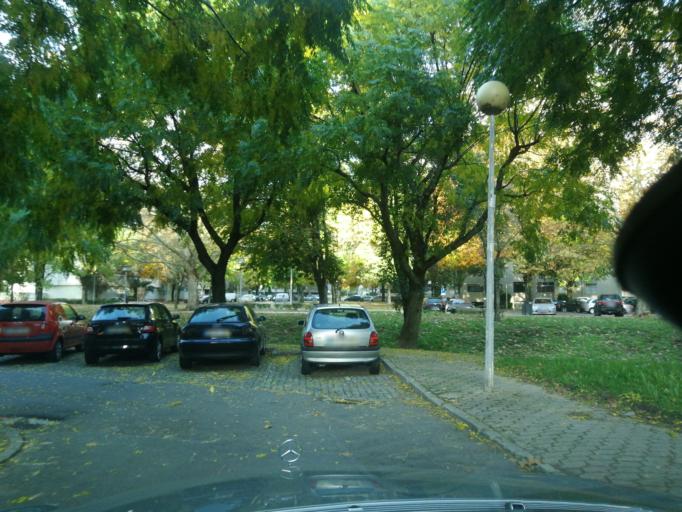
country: PT
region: Braga
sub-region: Braga
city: Braga
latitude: 41.5463
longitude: -8.4112
